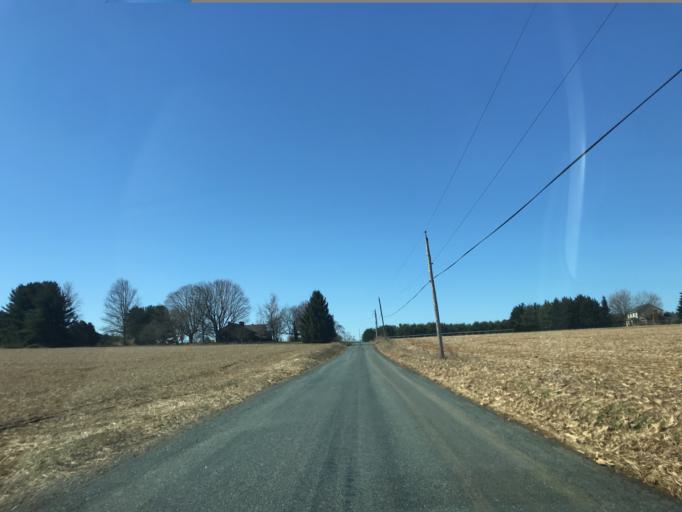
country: US
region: Pennsylvania
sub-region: York County
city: Stewartstown
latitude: 39.7098
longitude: -76.5302
